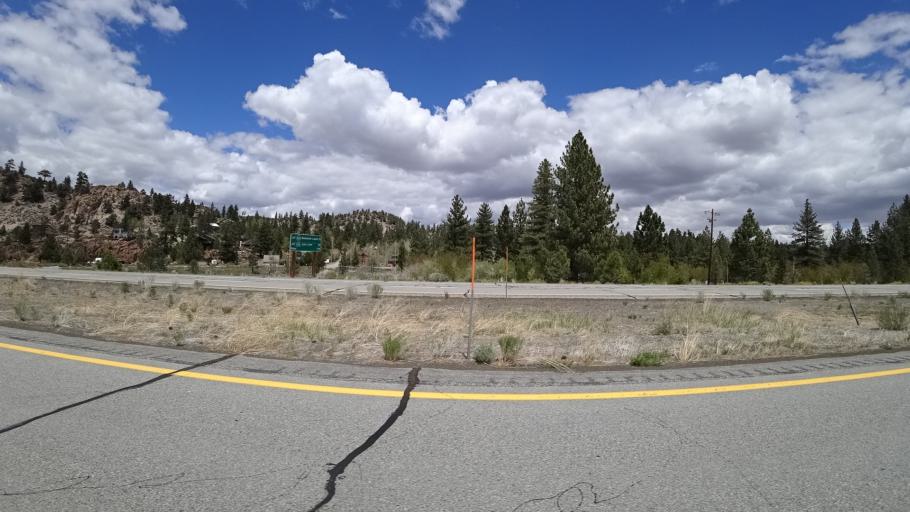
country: US
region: California
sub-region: Mono County
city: Mammoth Lakes
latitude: 37.5633
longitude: -118.6818
